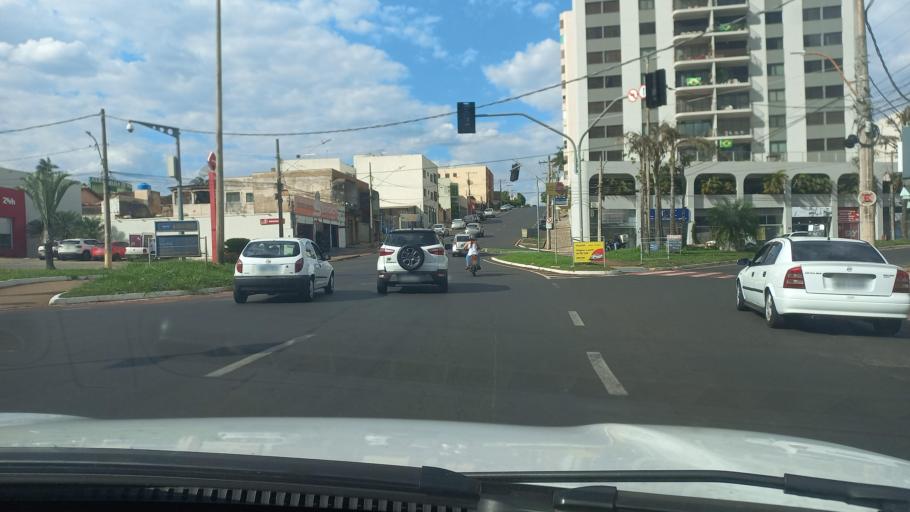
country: BR
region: Minas Gerais
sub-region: Uberaba
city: Uberaba
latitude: -19.7433
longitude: -47.9317
